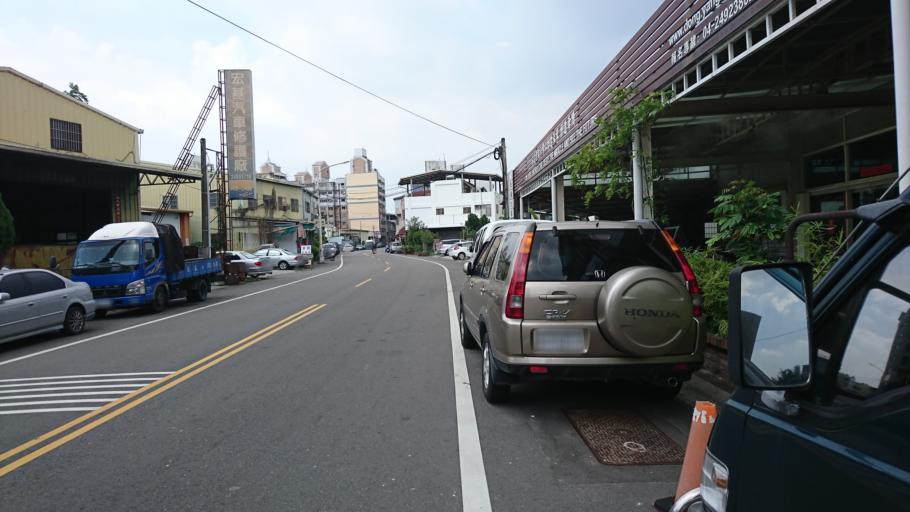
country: TW
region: Taiwan
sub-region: Taichung City
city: Taichung
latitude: 24.0781
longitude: 120.6911
